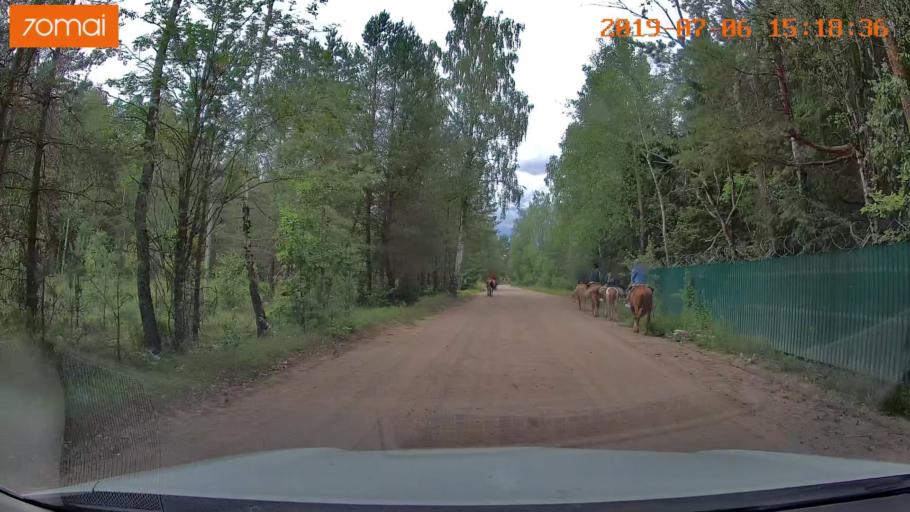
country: BY
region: Minsk
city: Ivyanyets
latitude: 53.9929
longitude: 26.6518
